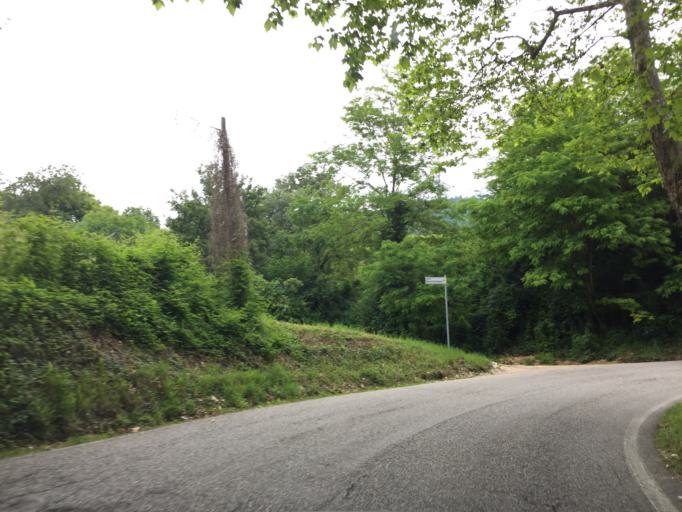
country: IT
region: Veneto
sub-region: Provincia di Treviso
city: Valdobbiadene
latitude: 45.8960
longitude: 11.9609
